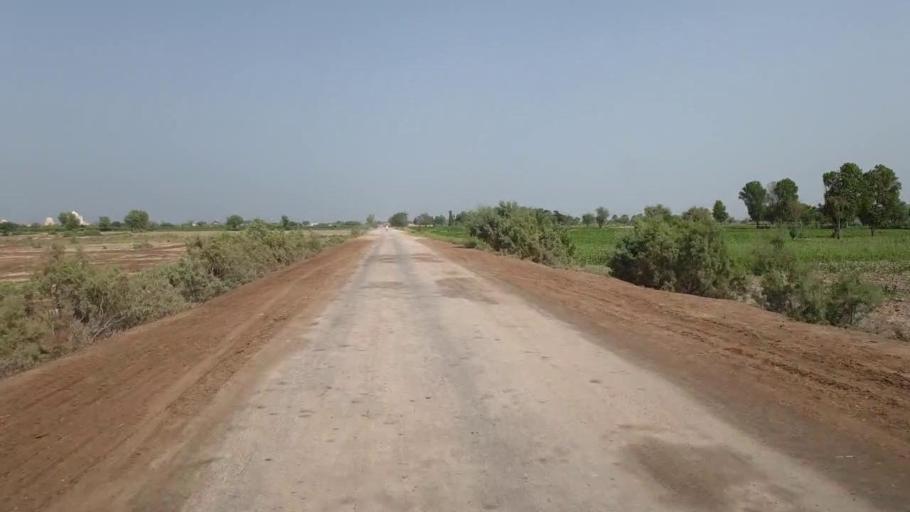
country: PK
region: Sindh
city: Daulatpur
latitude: 26.5507
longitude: 68.0565
